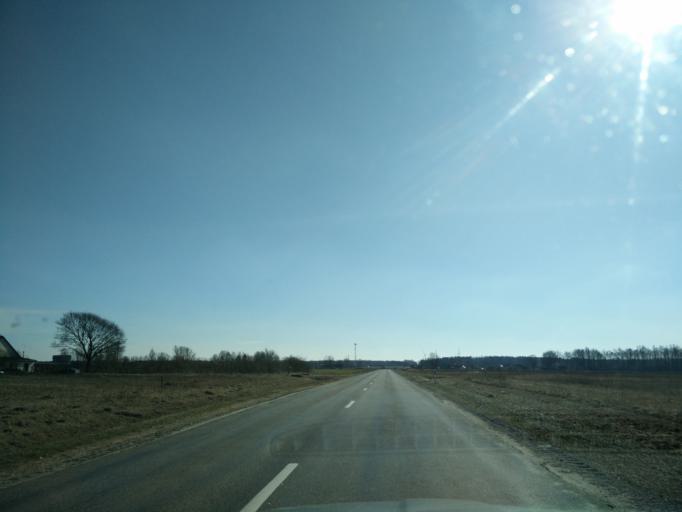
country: LT
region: Klaipedos apskritis
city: Silute
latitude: 55.3199
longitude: 21.5298
